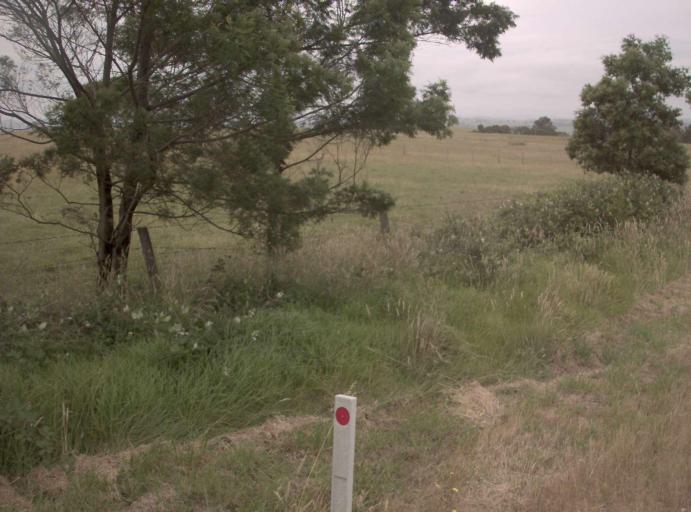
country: AU
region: Victoria
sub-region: East Gippsland
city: Bairnsdale
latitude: -37.8116
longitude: 147.4373
